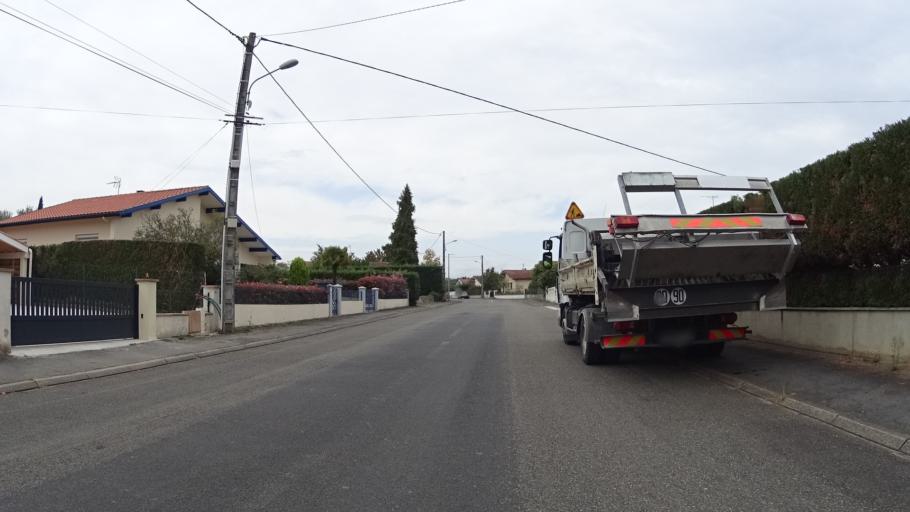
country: FR
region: Aquitaine
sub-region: Departement des Landes
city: Saint-Paul-les-Dax
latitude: 43.7272
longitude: -1.0703
